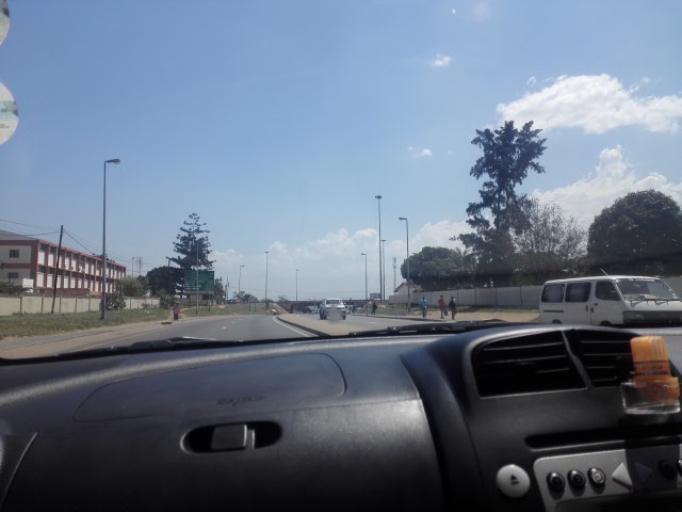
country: MZ
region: Maputo City
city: Maputo
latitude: -25.9421
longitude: 32.5433
